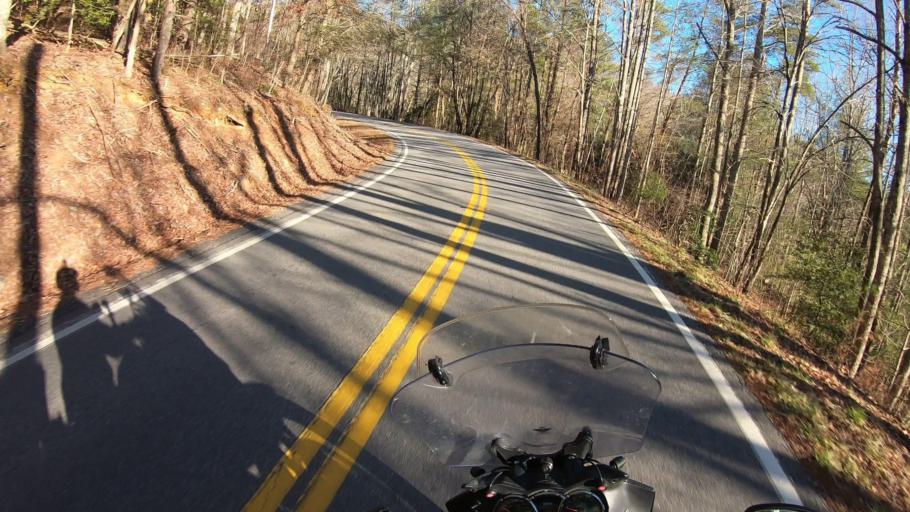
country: US
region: Georgia
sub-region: Lumpkin County
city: Dahlonega
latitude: 34.7049
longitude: -84.0672
